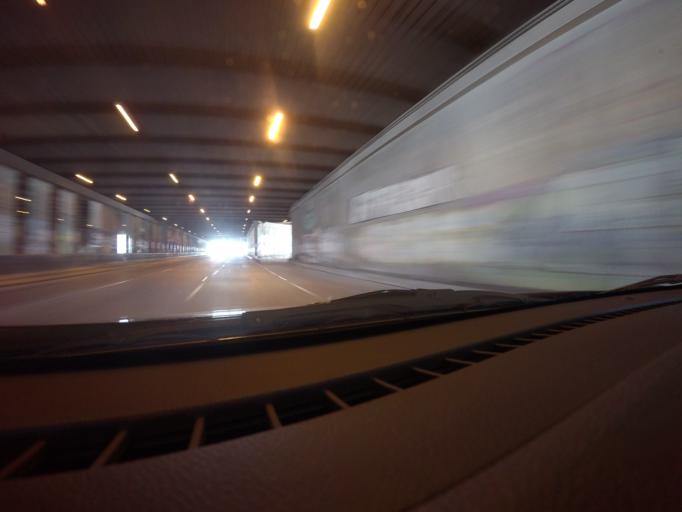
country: CO
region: Bogota D.C.
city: Bogota
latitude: 4.6238
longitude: -74.0788
